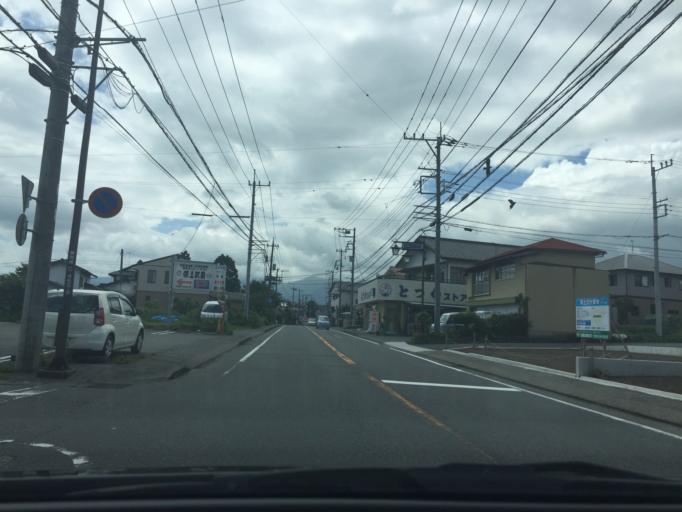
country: JP
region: Shizuoka
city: Gotemba
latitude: 35.2952
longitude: 138.9011
